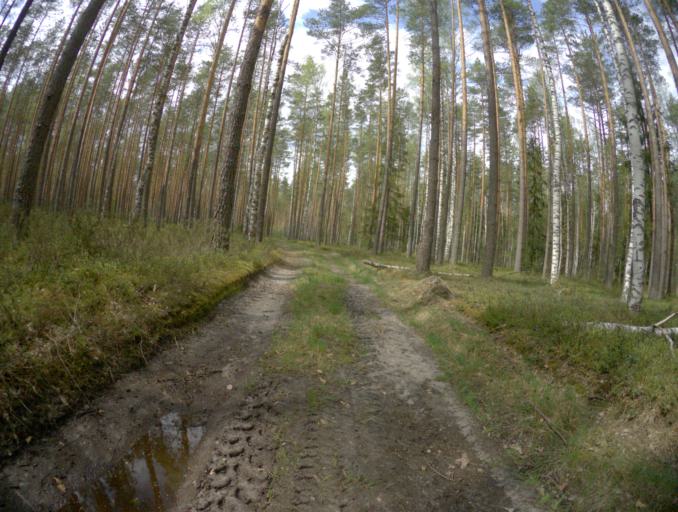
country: RU
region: Vladimir
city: Golovino
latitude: 55.9294
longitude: 40.3809
